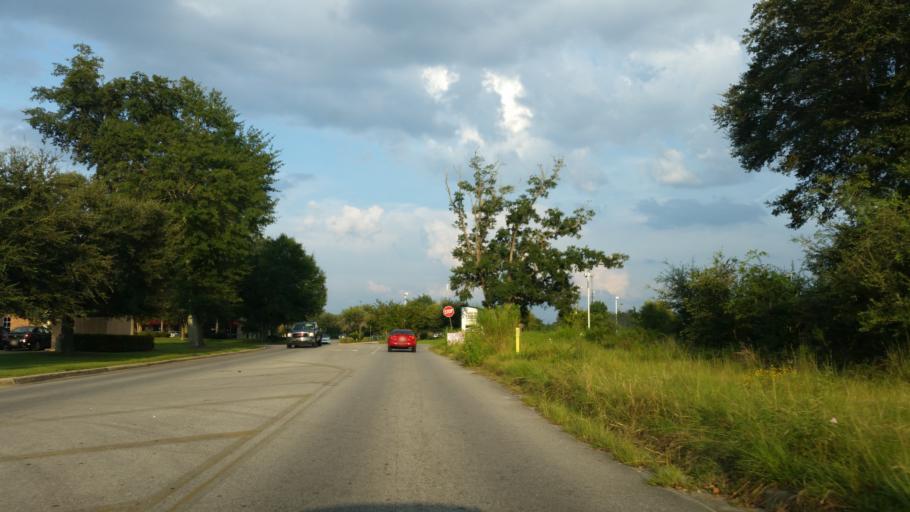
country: US
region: Florida
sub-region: Santa Rosa County
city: Pace
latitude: 30.6024
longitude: -87.1211
